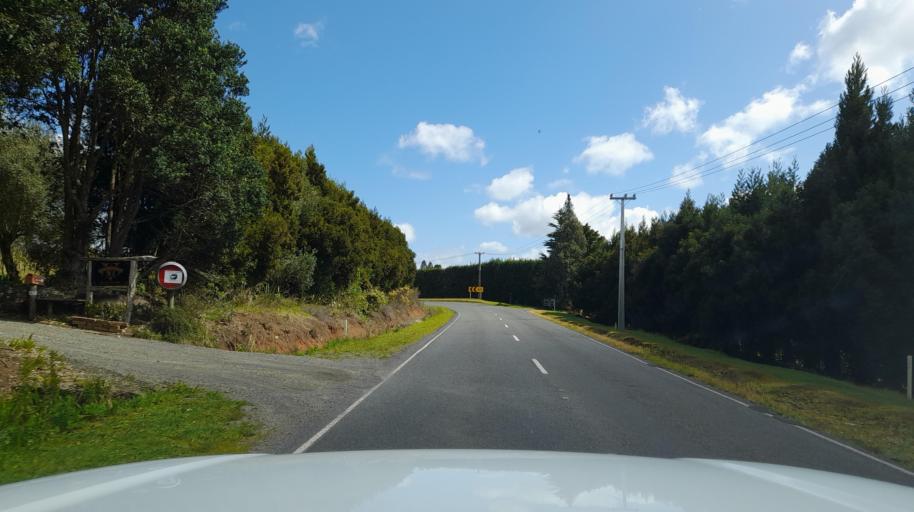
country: NZ
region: Northland
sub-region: Far North District
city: Kerikeri
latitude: -35.2327
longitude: 173.9056
